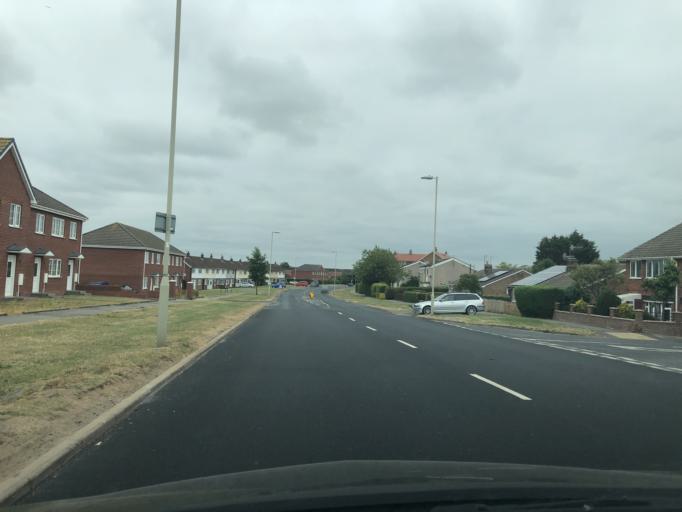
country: GB
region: England
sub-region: North Yorkshire
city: Scarborough
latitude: 54.2415
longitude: -0.3929
